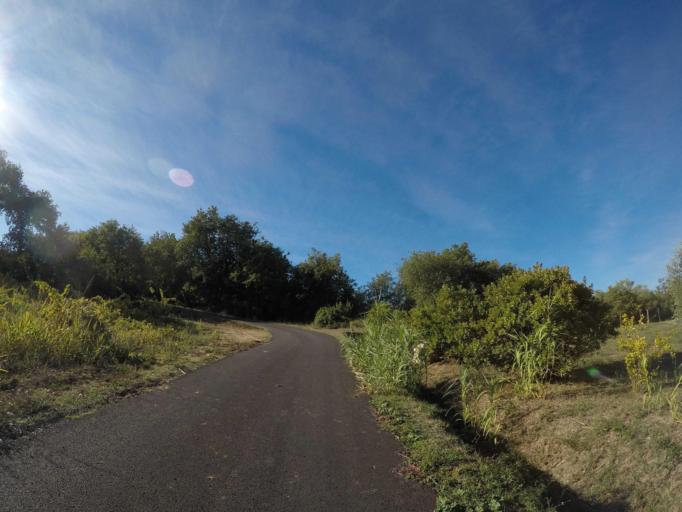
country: FR
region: Languedoc-Roussillon
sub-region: Departement des Pyrenees-Orientales
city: Trouillas
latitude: 42.5785
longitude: 2.7843
